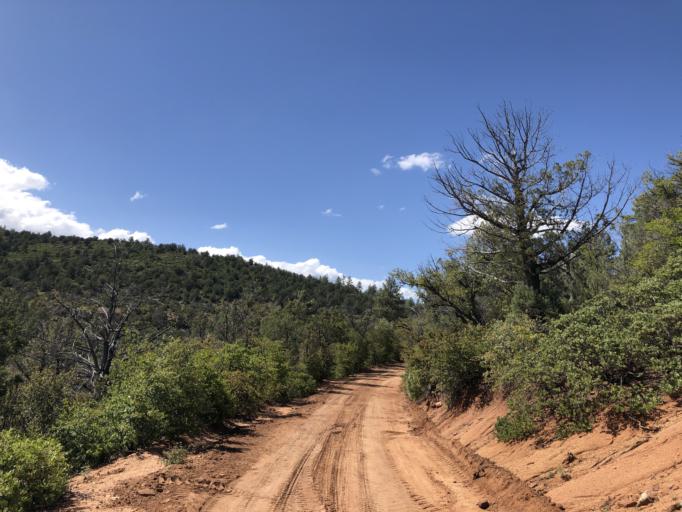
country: US
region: Arizona
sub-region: Gila County
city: Star Valley
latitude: 34.3564
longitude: -111.2810
